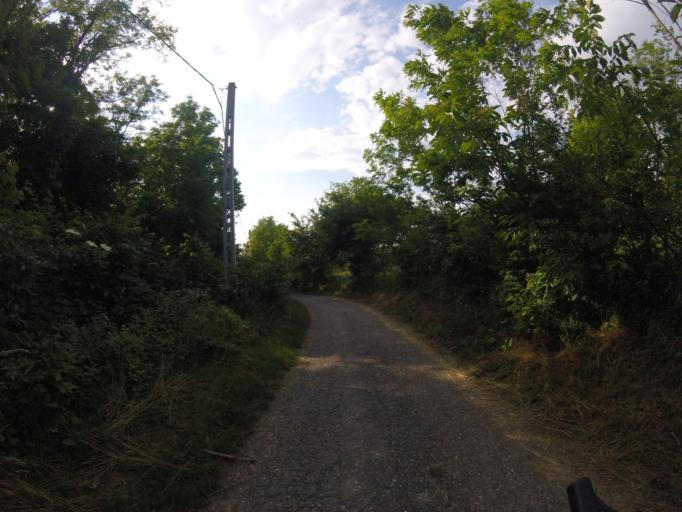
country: HU
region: Zala
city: Zalaszentgrot
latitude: 46.8860
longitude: 17.1264
